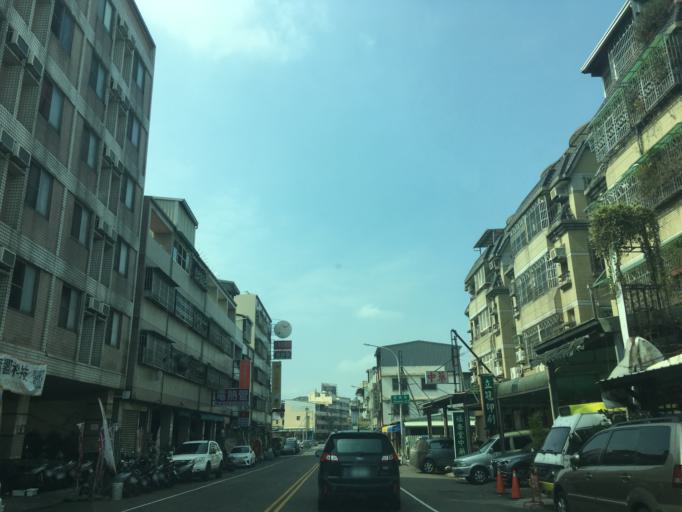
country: TW
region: Taiwan
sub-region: Taichung City
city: Taichung
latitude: 24.1340
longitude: 120.7057
